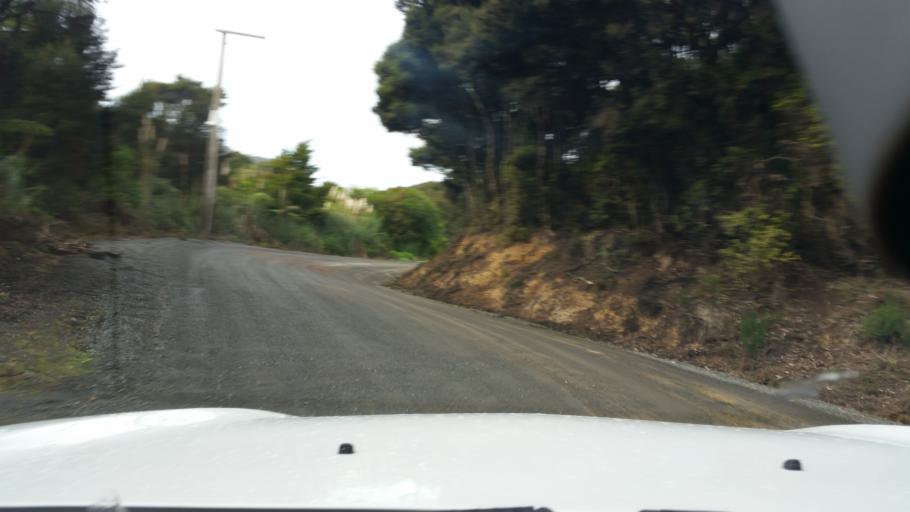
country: NZ
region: Northland
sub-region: Whangarei
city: Ngunguru
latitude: -35.7691
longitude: 174.5312
